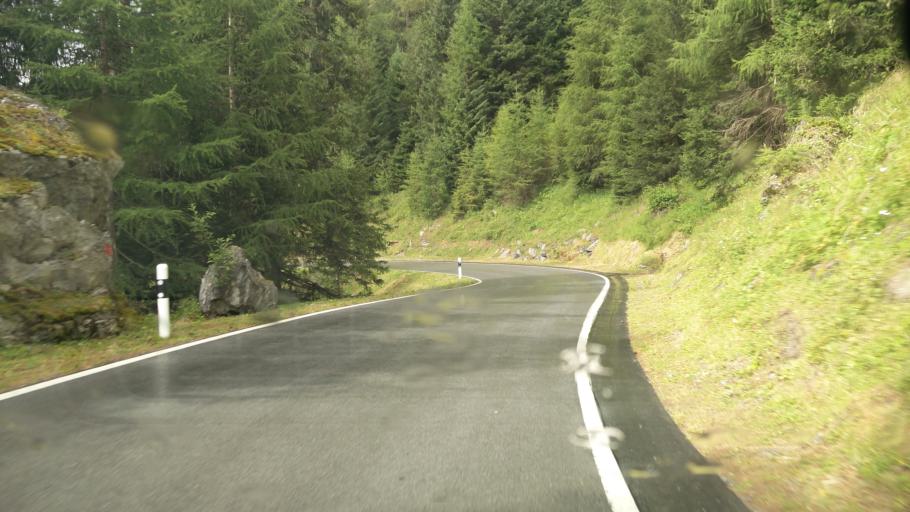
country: IT
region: Trentino-Alto Adige
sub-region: Bolzano
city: Tubre
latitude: 46.5831
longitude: 10.4368
